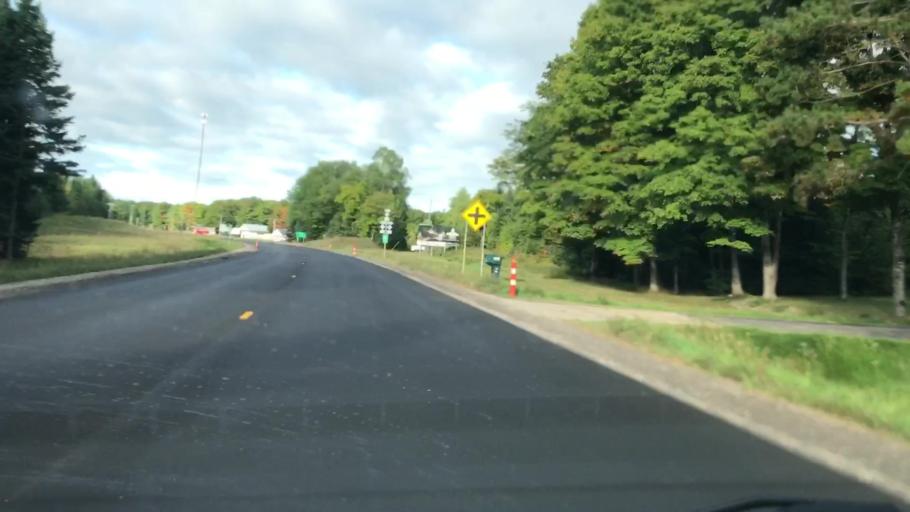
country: US
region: Michigan
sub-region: Luce County
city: Newberry
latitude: 46.3464
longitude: -85.0259
